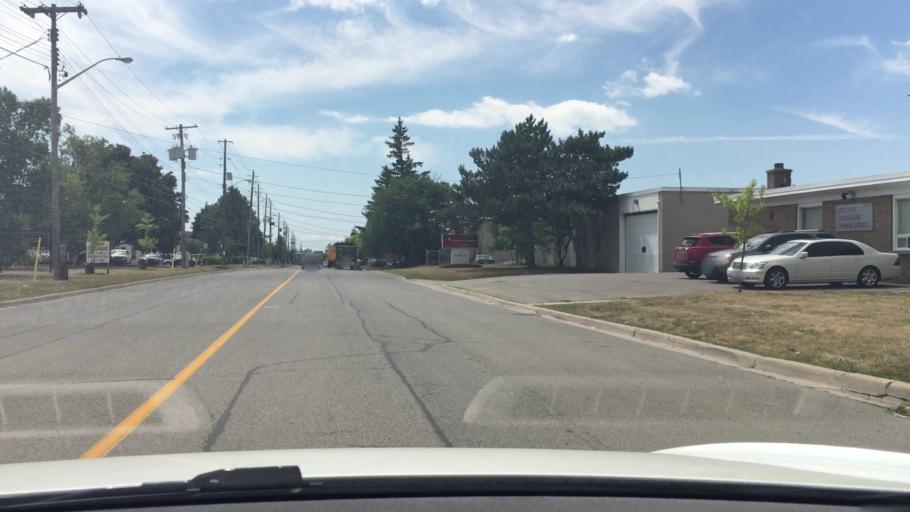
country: CA
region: Ontario
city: Scarborough
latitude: 43.7514
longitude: -79.2899
